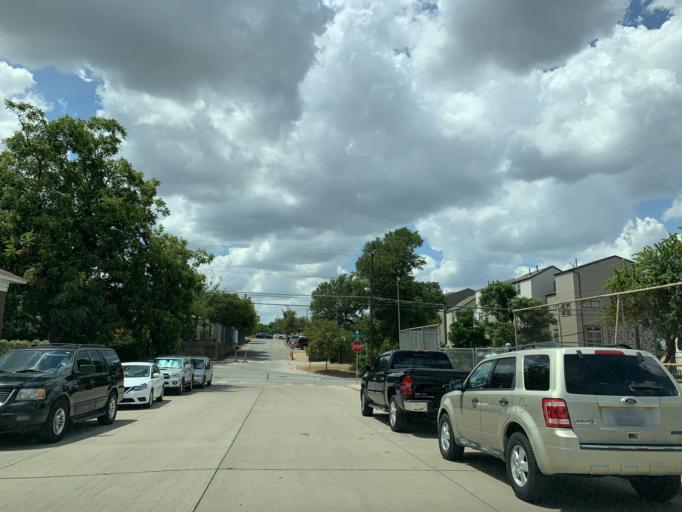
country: US
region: Texas
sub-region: Dallas County
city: Cockrell Hill
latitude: 32.7509
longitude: -96.8477
